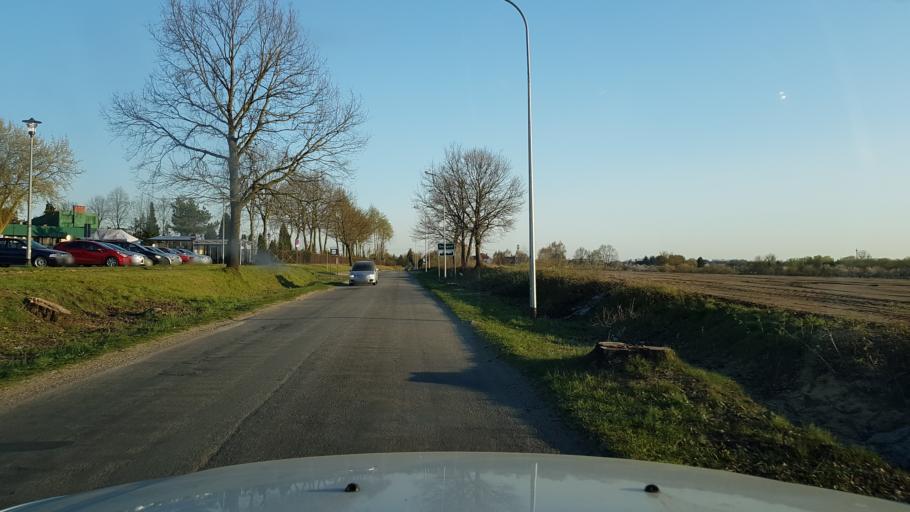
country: PL
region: West Pomeranian Voivodeship
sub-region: Powiat bialogardzki
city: Bialogard
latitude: 54.0233
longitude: 15.9876
